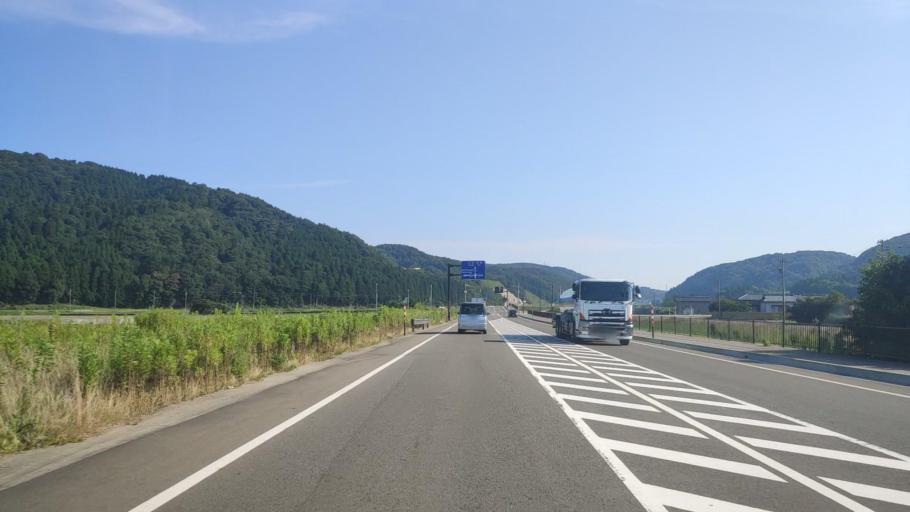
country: JP
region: Fukui
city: Maruoka
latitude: 36.2006
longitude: 136.2674
